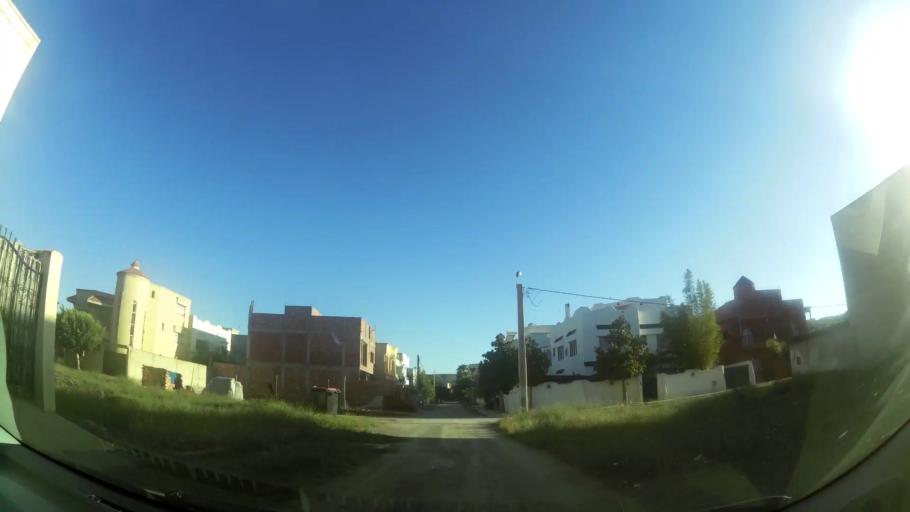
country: MA
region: Oriental
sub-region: Berkane-Taourirt
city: Madagh
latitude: 35.0883
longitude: -2.2465
